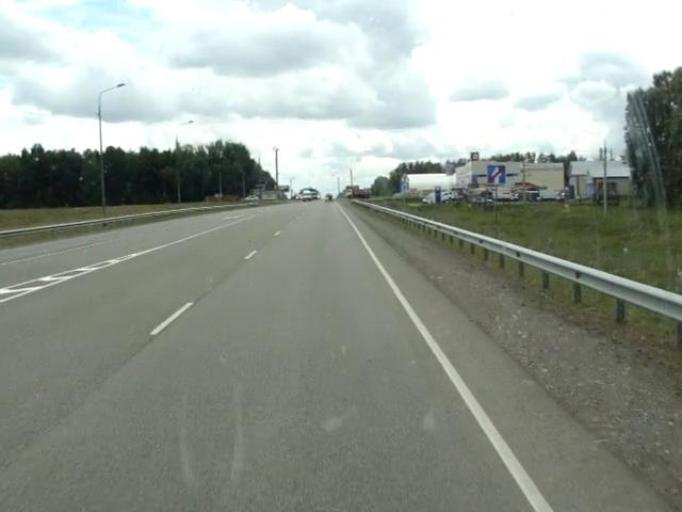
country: RU
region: Altai Krai
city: Zarya
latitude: 52.5767
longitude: 85.1791
